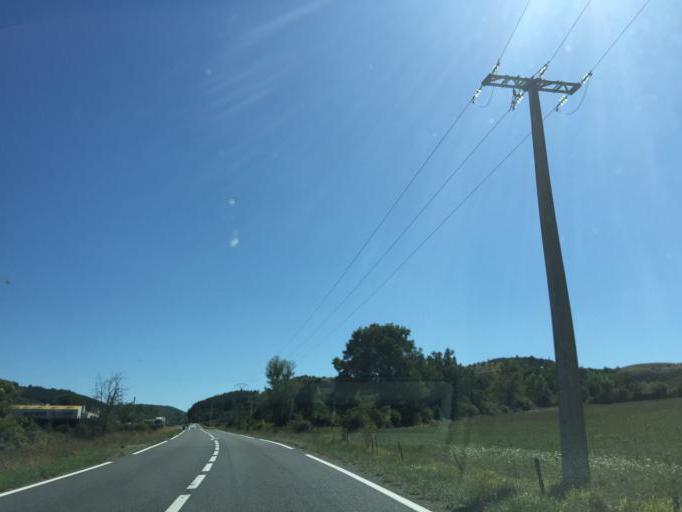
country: FR
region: Midi-Pyrenees
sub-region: Departement de l'Aveyron
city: Saint-Georges-de-Luzencon
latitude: 43.9934
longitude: 2.9677
